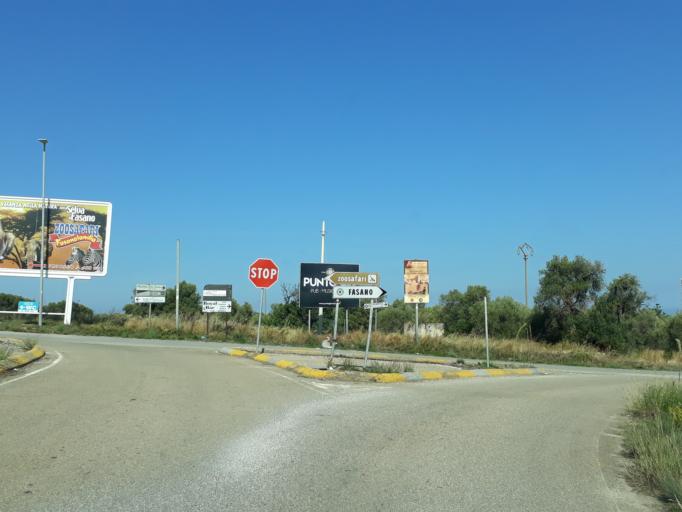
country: IT
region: Apulia
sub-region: Provincia di Brindisi
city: Fasano
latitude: 40.8336
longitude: 17.3483
